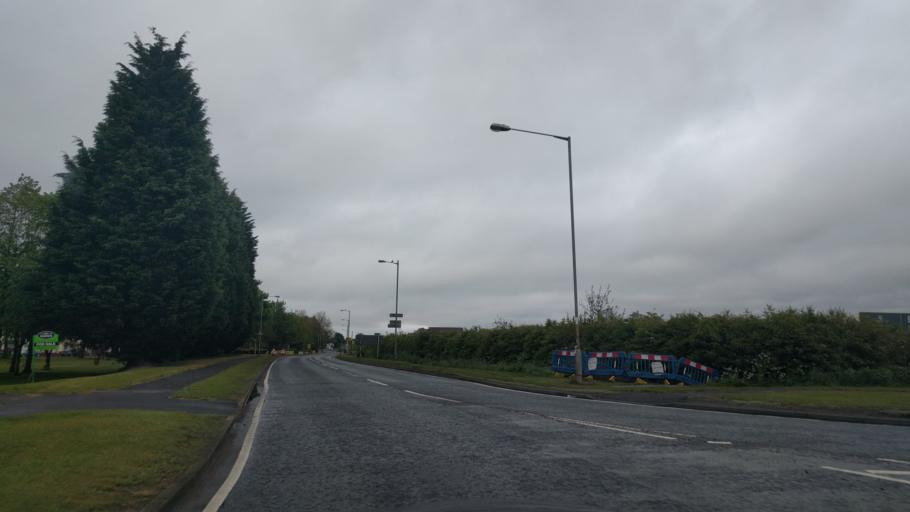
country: GB
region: England
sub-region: Northumberland
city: Morpeth
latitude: 55.1567
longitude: -1.6755
